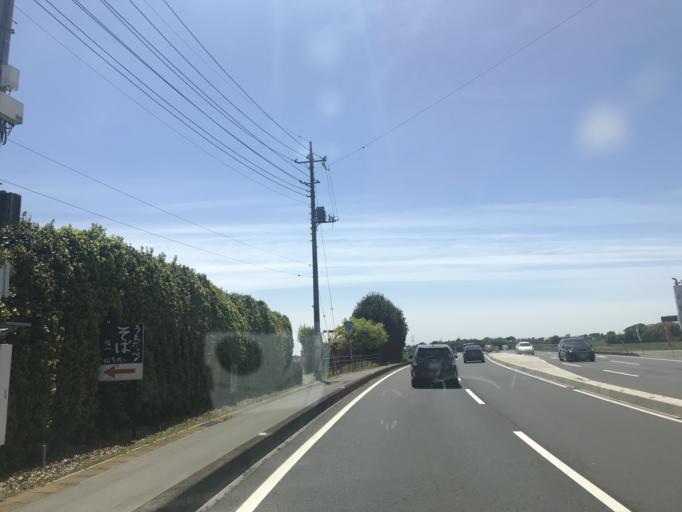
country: JP
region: Ibaraki
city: Shimodate
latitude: 36.2625
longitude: 139.9839
